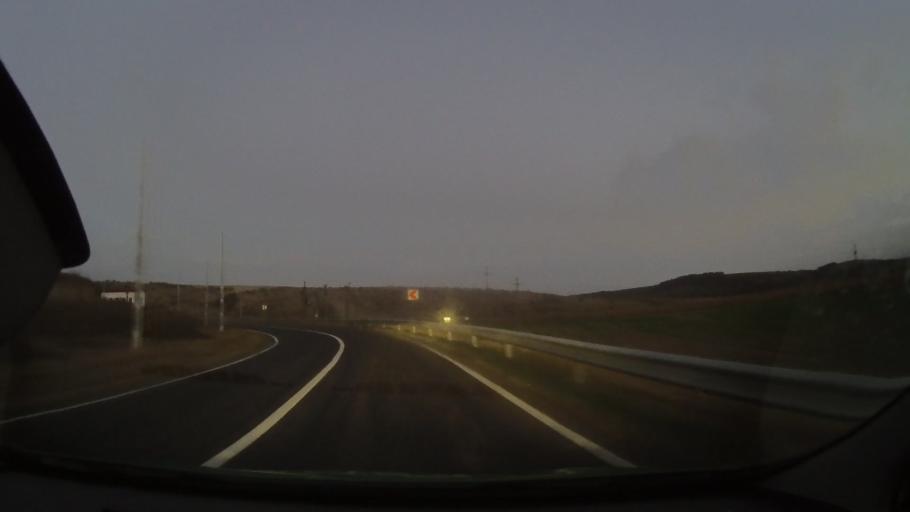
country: RO
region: Constanta
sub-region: Comuna Ion Corvin
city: Ion Corvin
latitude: 44.1008
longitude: 27.7972
